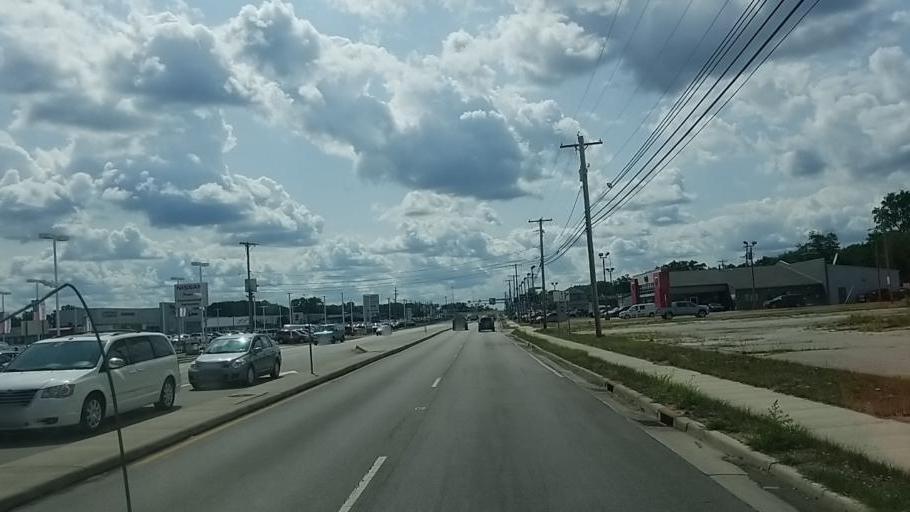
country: US
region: Ohio
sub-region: Lucas County
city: Ottawa Hills
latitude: 41.6763
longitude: -83.6841
